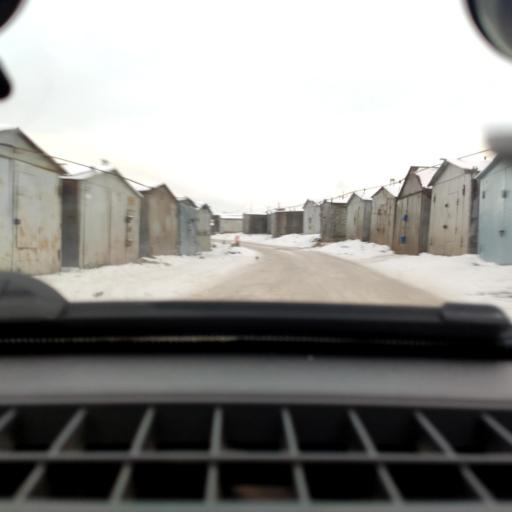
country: RU
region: Bashkortostan
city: Ufa
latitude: 54.8071
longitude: 56.1403
